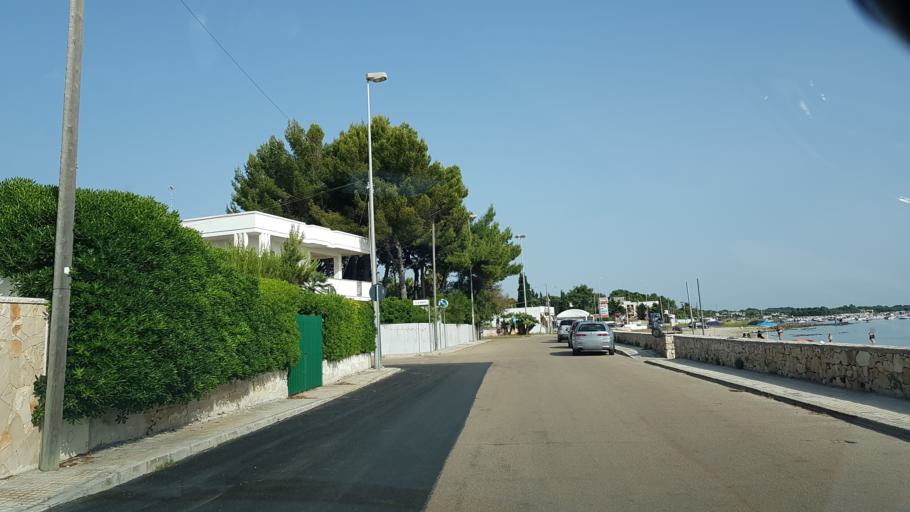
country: IT
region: Apulia
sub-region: Provincia di Lecce
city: Porto Cesareo
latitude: 40.2570
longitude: 17.9039
